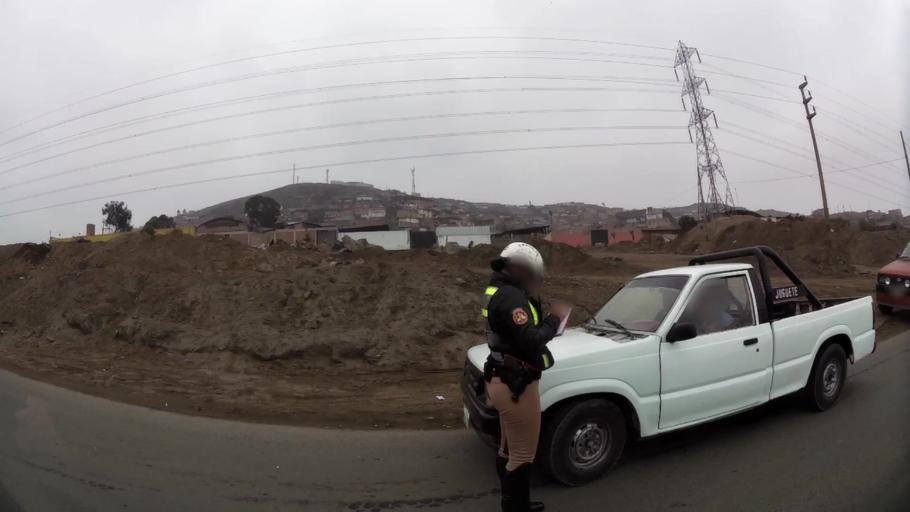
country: PE
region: Lima
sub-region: Lima
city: Surco
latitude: -12.2119
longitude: -76.9239
